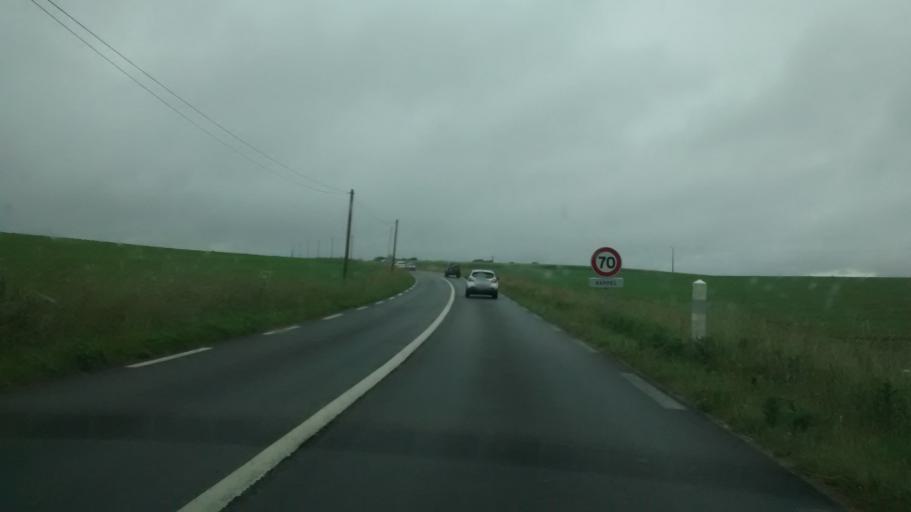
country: FR
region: Brittany
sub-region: Departement du Morbihan
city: Ploemeur
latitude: 47.7451
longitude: -3.4204
